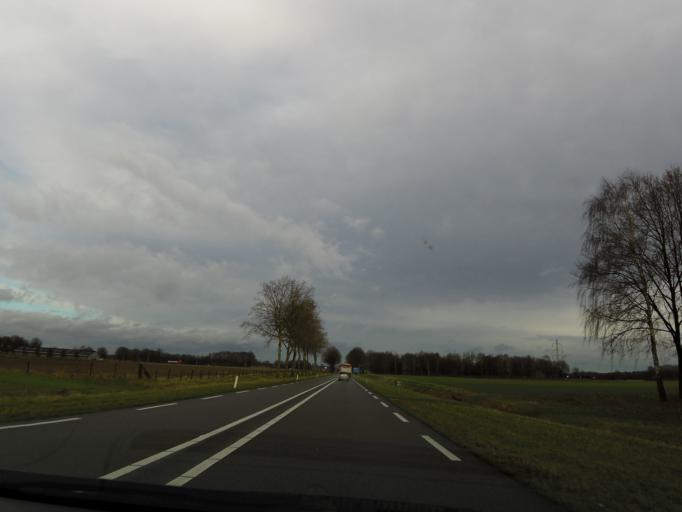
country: NL
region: Limburg
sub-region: Gemeente Roerdalen
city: Posterholt
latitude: 51.1175
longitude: 6.0453
